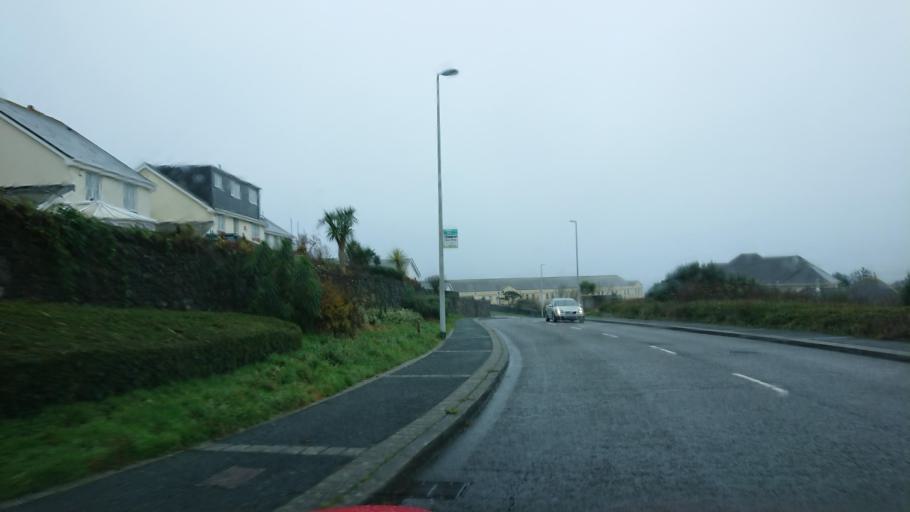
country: GB
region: England
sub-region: Plymouth
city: Plymouth
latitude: 50.3570
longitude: -4.1222
